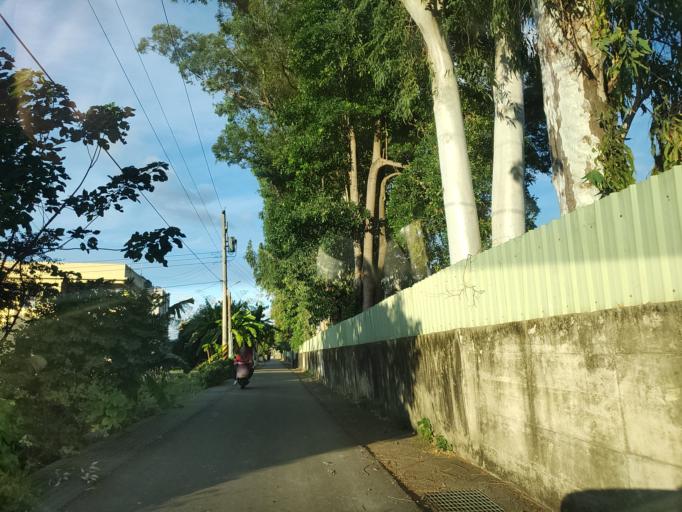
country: TW
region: Taiwan
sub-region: Miaoli
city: Miaoli
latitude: 24.5560
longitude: 120.8314
